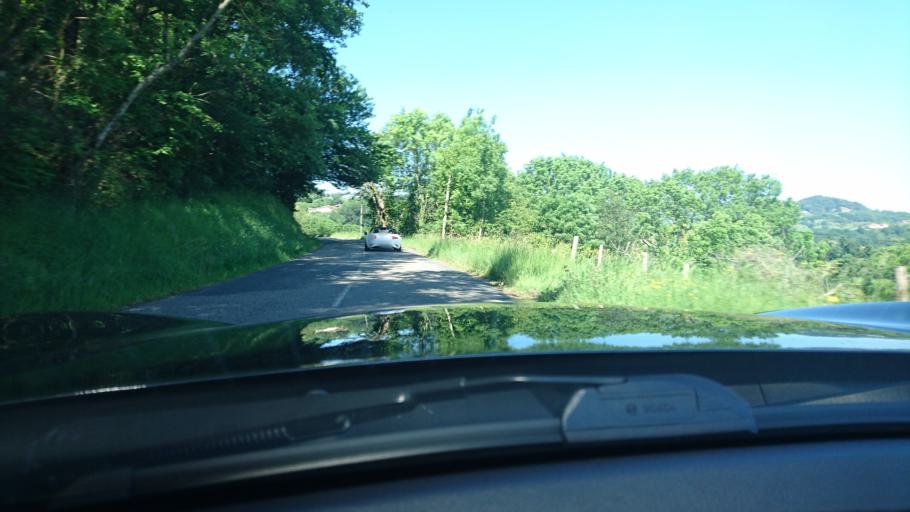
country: FR
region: Rhone-Alpes
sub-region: Departement du Rhone
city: Montrottier
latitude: 45.7860
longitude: 4.4956
